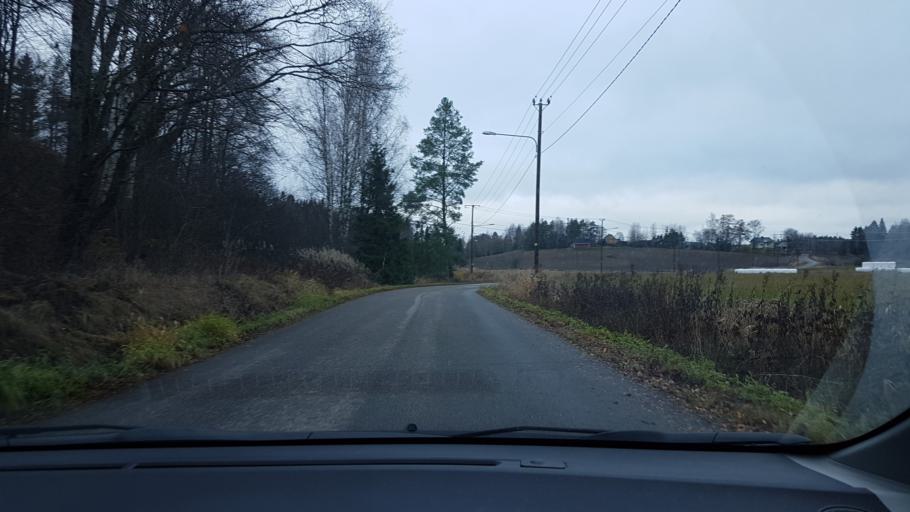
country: FI
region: Uusimaa
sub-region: Helsinki
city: Vantaa
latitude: 60.2784
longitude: 25.1365
